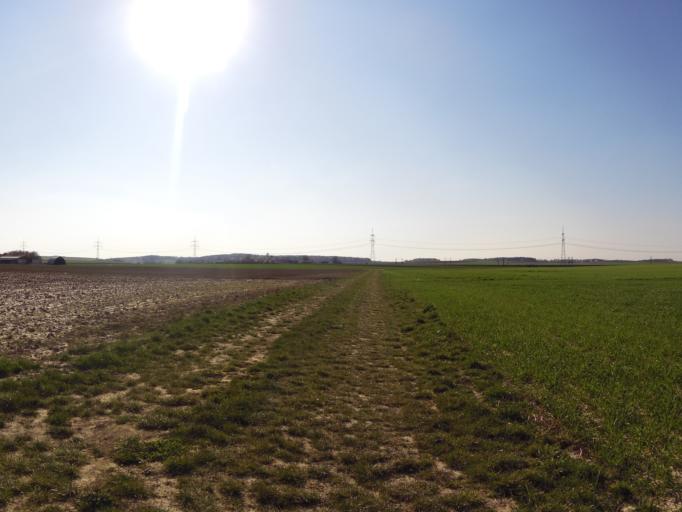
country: DE
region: Bavaria
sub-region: Regierungsbezirk Unterfranken
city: Prosselsheim
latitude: 49.8361
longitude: 10.1032
